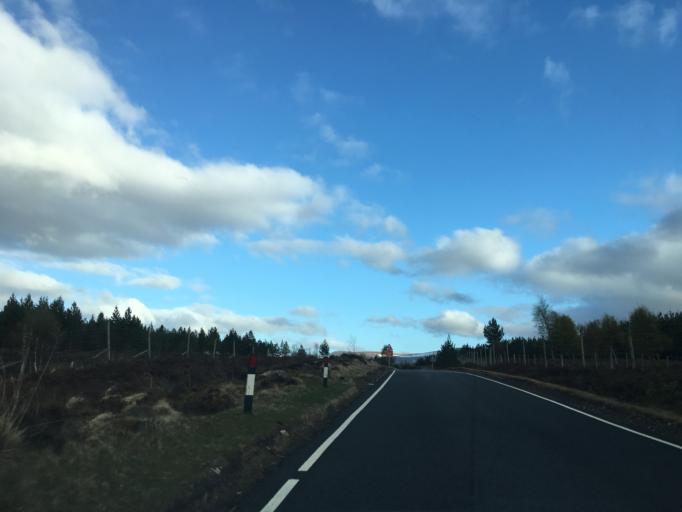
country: GB
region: Scotland
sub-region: Highland
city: Kingussie
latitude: 56.9875
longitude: -4.2431
